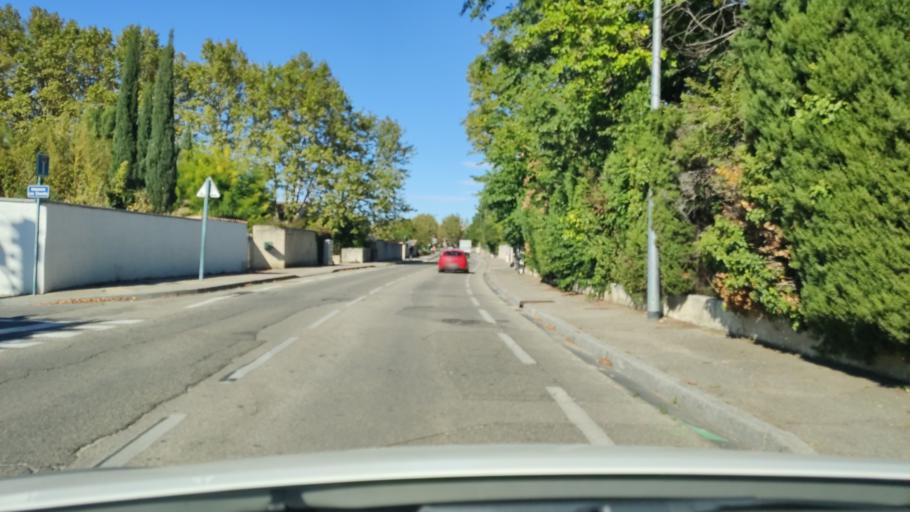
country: FR
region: Provence-Alpes-Cote d'Azur
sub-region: Departement du Vaucluse
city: Morieres-les-Avignon
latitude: 43.9378
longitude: 4.9023
